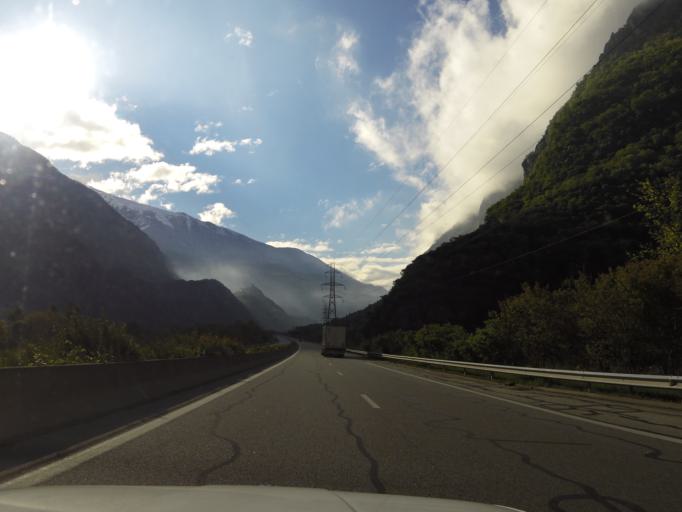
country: FR
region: Rhone-Alpes
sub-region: Departement de la Savoie
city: Saint-Jean-de-Maurienne
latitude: 45.3173
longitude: 6.3254
